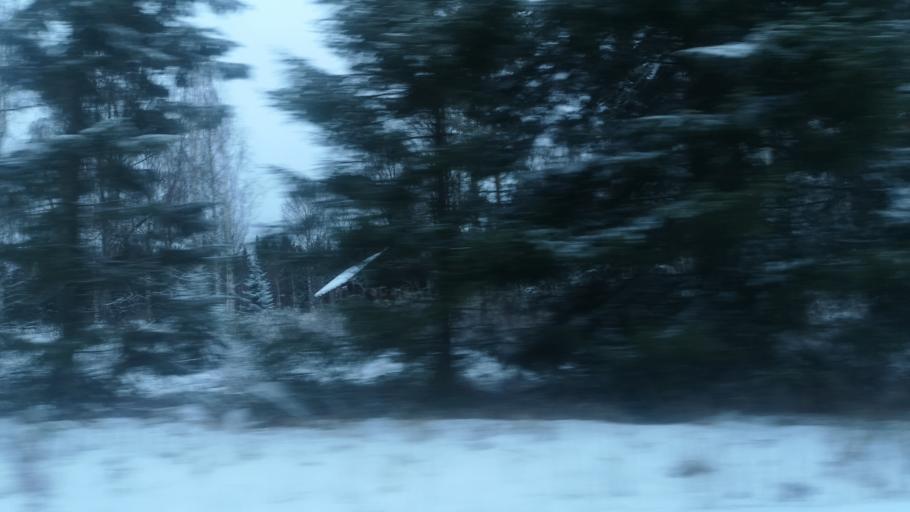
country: FI
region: Southern Savonia
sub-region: Savonlinna
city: Enonkoski
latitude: 62.0330
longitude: 28.7185
